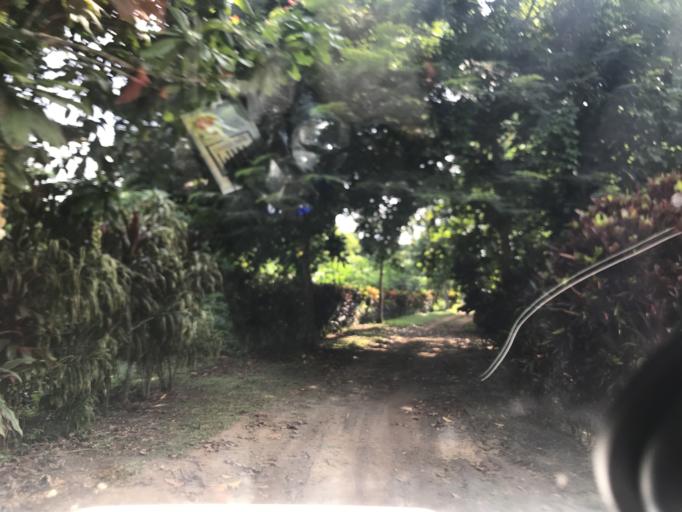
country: VU
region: Sanma
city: Luganville
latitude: -15.3130
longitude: 167.1692
